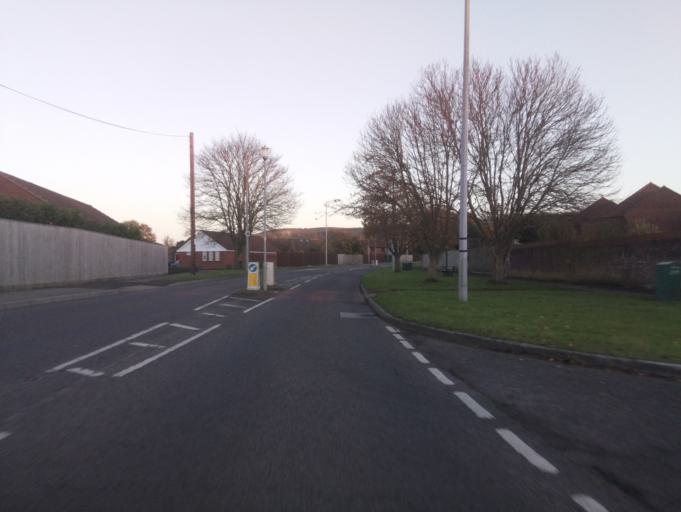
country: GB
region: England
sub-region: Wiltshire
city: Westbury
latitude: 51.2659
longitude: -2.1760
